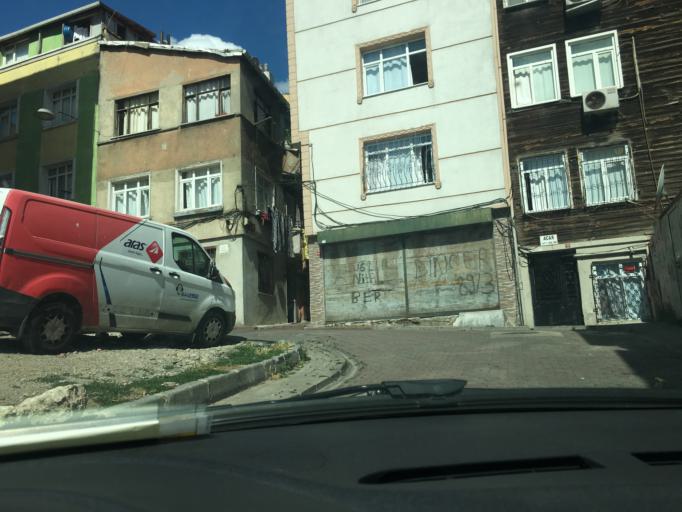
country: TR
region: Istanbul
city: Istanbul
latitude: 41.0212
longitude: 28.9570
